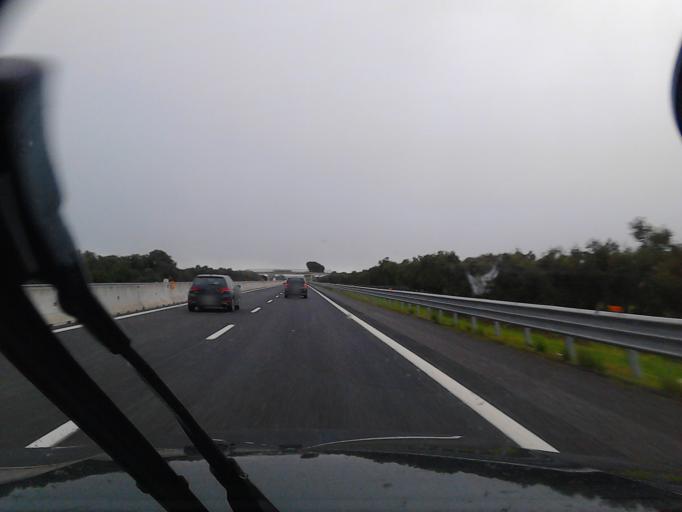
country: IT
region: Apulia
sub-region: Provincia di Bari
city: Giovinazzo
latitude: 41.1491
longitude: 16.6660
